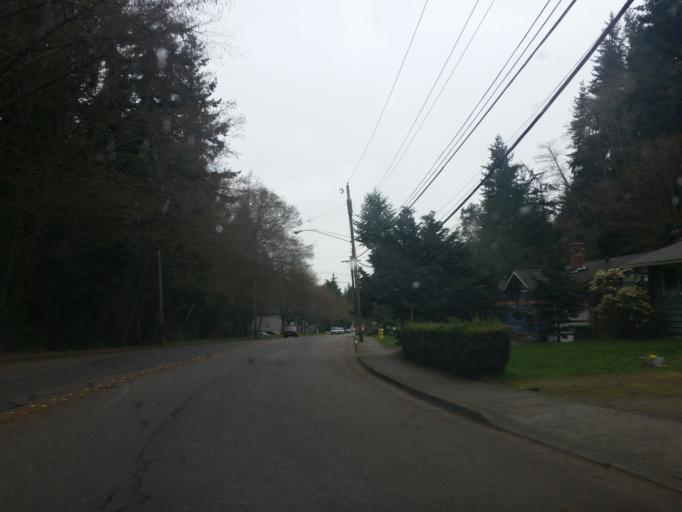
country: US
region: Washington
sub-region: Snohomish County
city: Lynnwood
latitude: 47.8275
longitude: -122.3374
